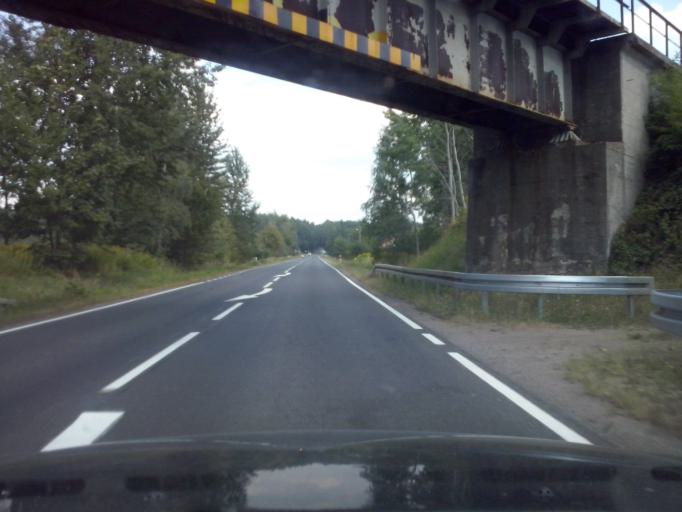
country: PL
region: Swietokrzyskie
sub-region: Powiat staszowski
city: Osiek
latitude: 50.5285
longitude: 21.4778
